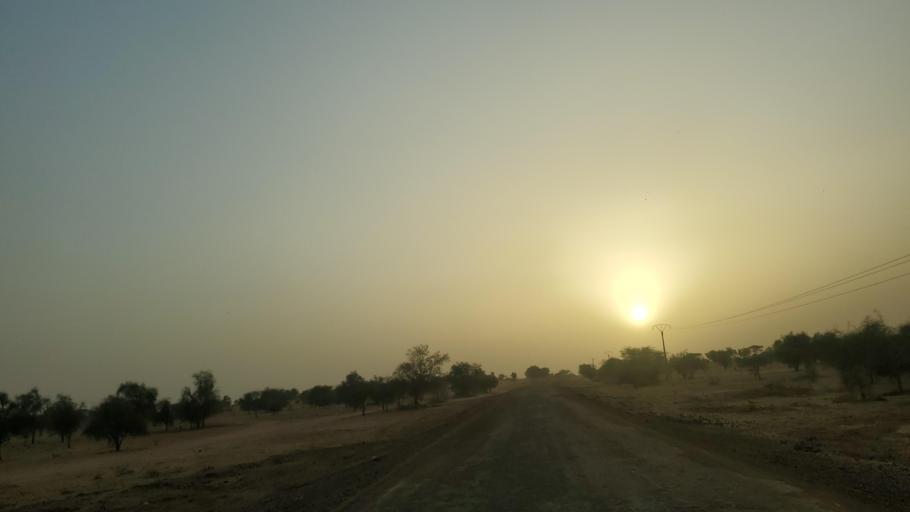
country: SN
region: Louga
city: Dara
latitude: 15.4142
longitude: -15.7059
